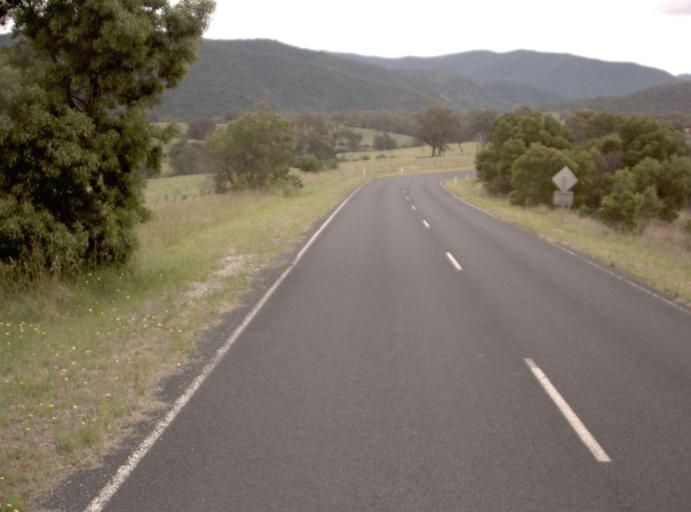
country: AU
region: Victoria
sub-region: East Gippsland
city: Bairnsdale
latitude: -37.5677
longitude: 147.1868
